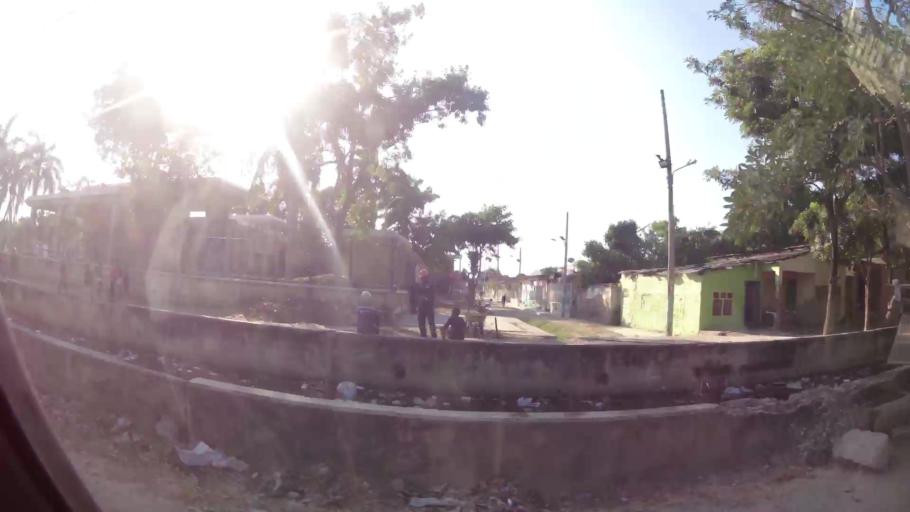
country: CO
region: Bolivar
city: Cartagena
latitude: 10.4104
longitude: -75.4987
